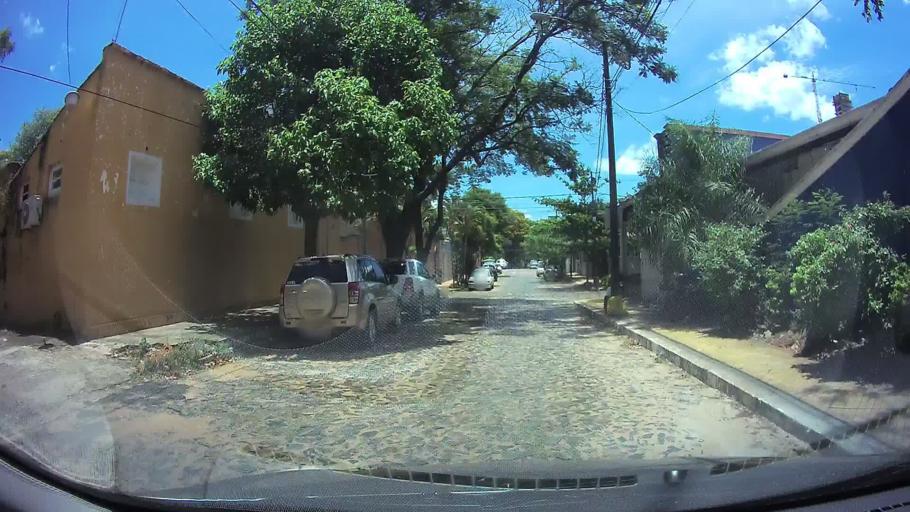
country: PY
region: Central
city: Lambare
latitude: -25.3016
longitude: -57.5683
